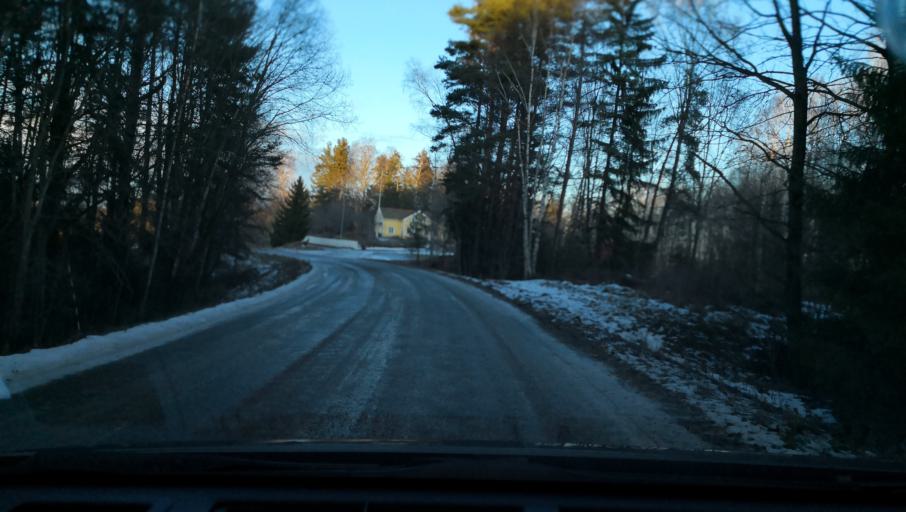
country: SE
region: Vaestmanland
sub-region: Vasteras
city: Tillberga
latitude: 59.7813
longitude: 16.6119
